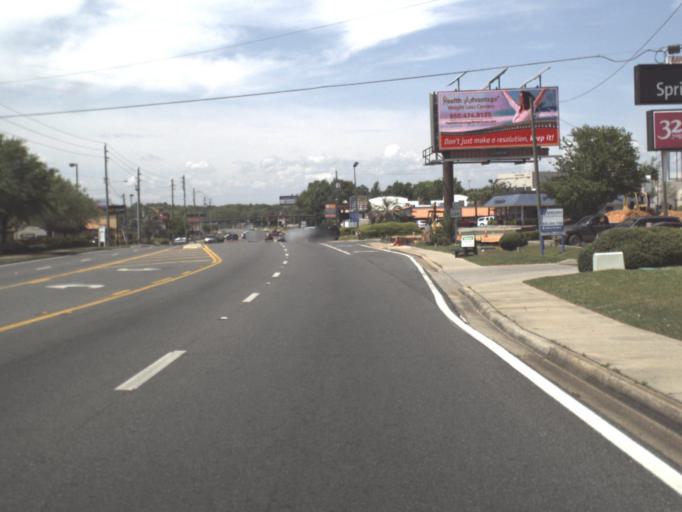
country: US
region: Florida
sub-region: Escambia County
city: Brent
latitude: 30.4723
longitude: -87.2097
